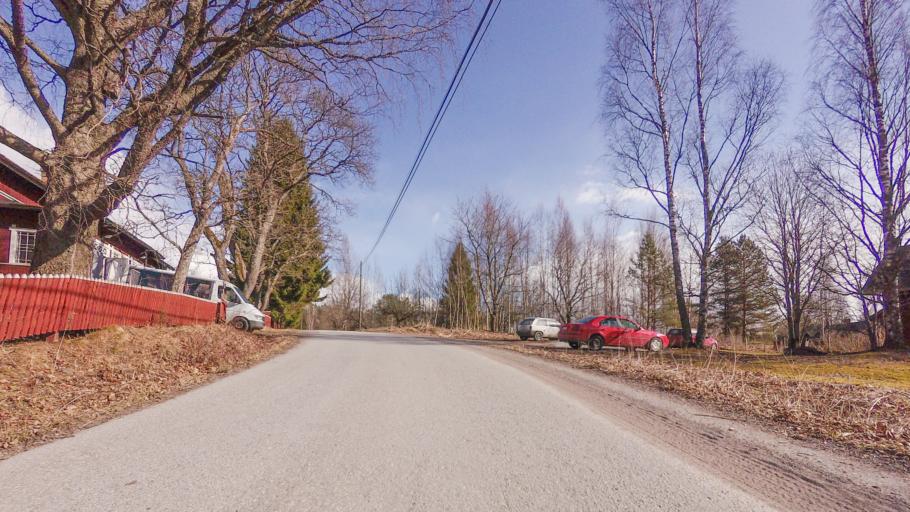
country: FI
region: Uusimaa
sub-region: Helsinki
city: Karjalohja
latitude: 60.2694
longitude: 23.6632
